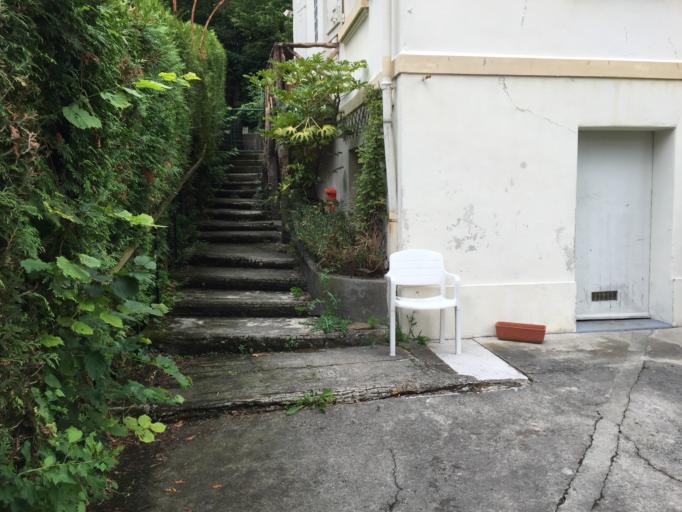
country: FR
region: Rhone-Alpes
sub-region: Departement de la Savoie
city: Jacob-Bellecombette
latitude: 45.5686
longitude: 5.9105
